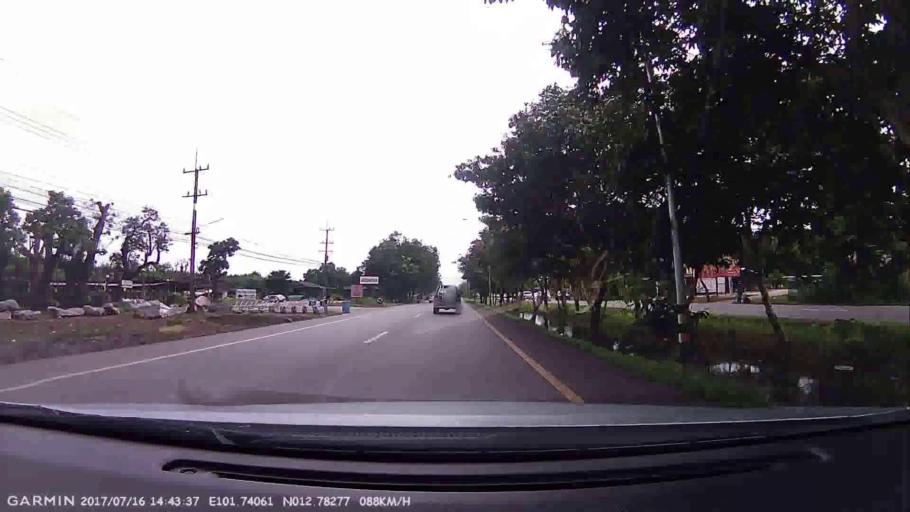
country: TH
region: Chanthaburi
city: Na Yai Am
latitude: 12.7827
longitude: 101.7403
